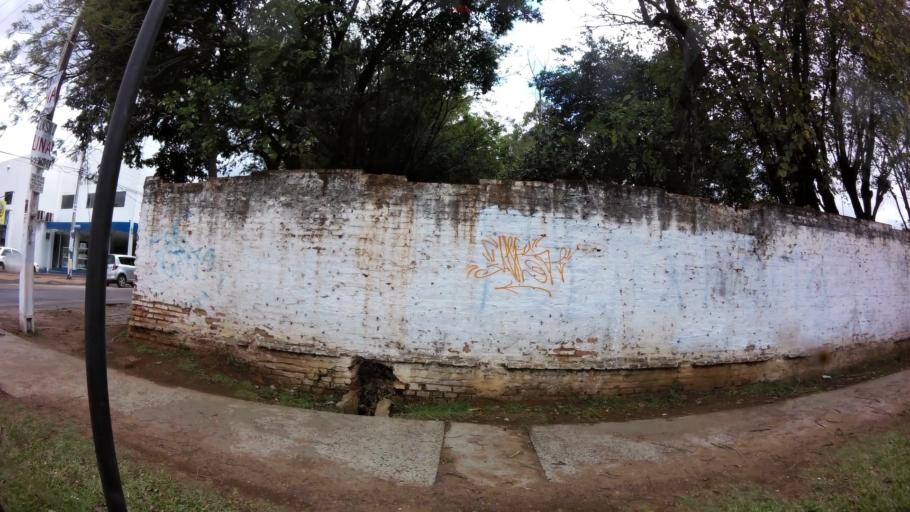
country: PY
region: Central
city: San Lorenzo
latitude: -25.2662
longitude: -57.4978
